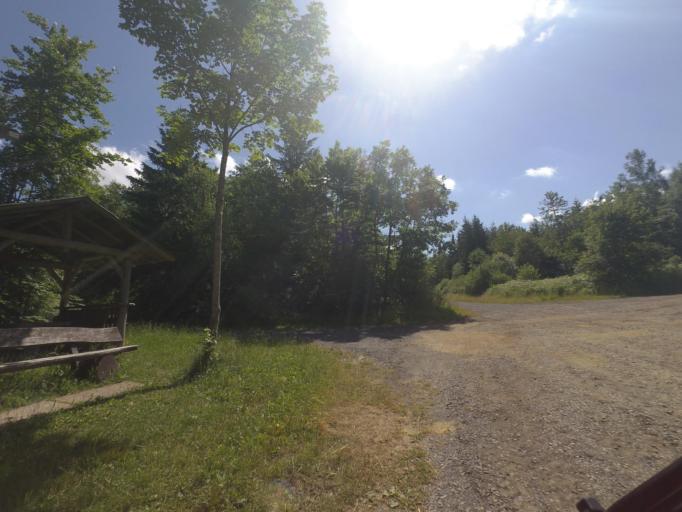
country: DE
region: Rheinland-Pfalz
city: Junkerath
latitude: 50.3226
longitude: 6.5591
